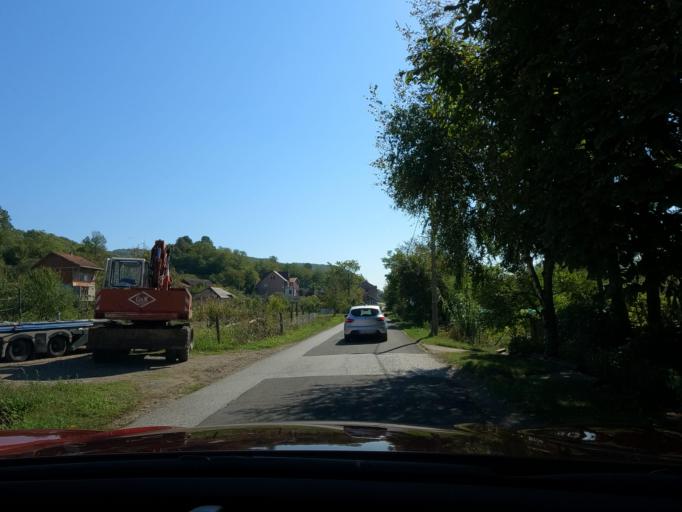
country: RS
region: Central Serbia
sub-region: Raski Okrug
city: Kraljevo
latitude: 43.7428
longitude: 20.7293
